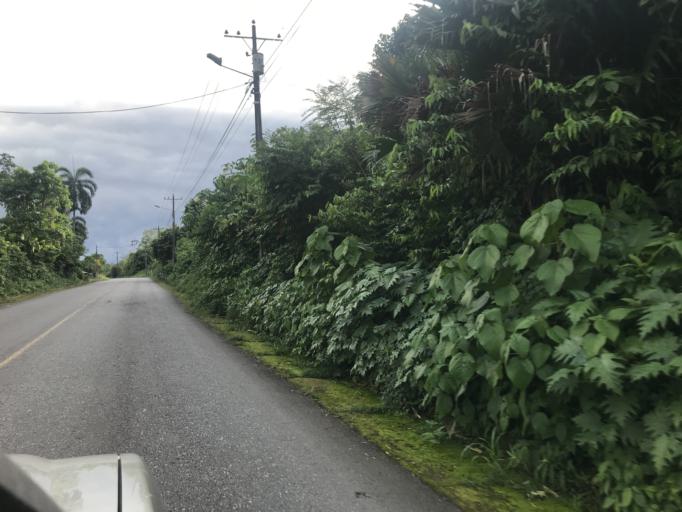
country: EC
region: Napo
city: Tena
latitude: -1.0366
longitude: -77.7559
